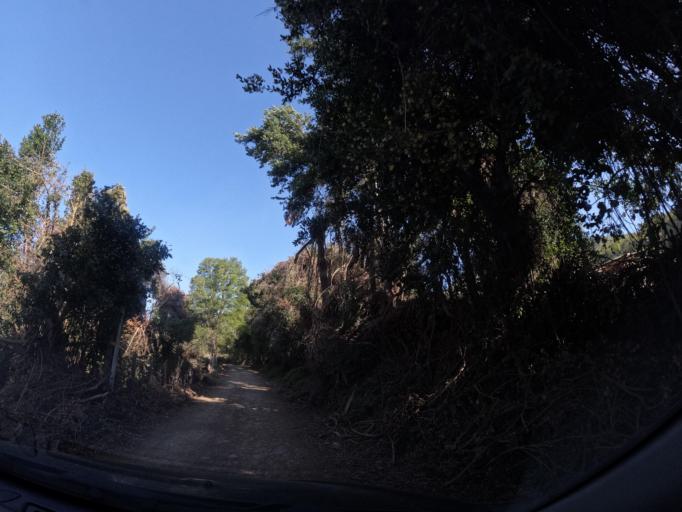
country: CL
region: Maule
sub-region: Provincia de Linares
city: Longavi
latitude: -36.2802
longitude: -71.4167
